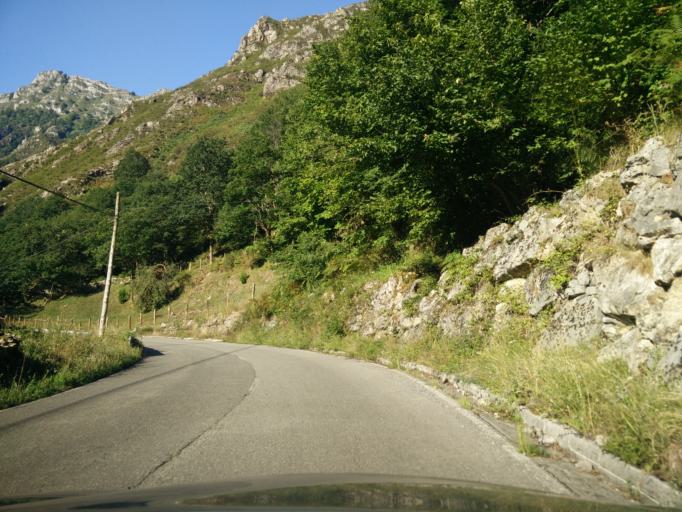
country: ES
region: Asturias
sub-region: Province of Asturias
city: Parres
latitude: 43.2392
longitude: -5.2071
